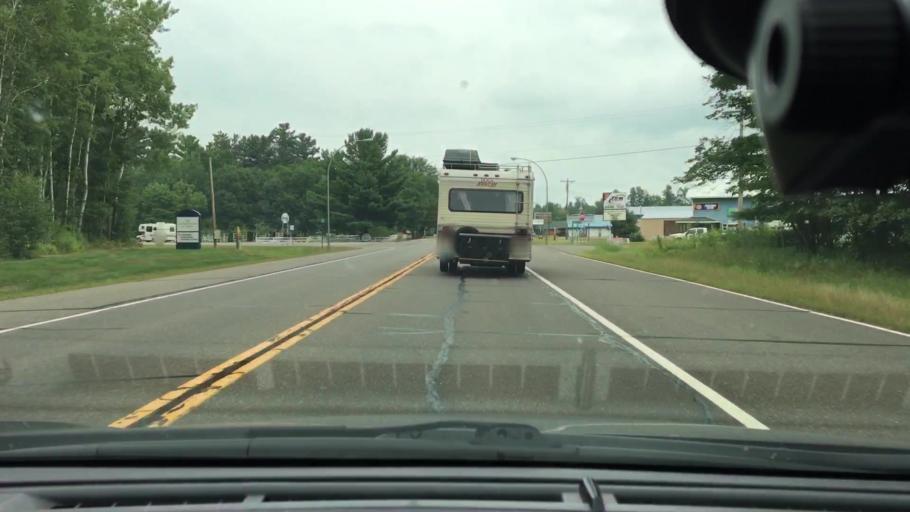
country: US
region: Minnesota
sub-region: Crow Wing County
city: Crosby
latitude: 46.4848
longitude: -93.9373
